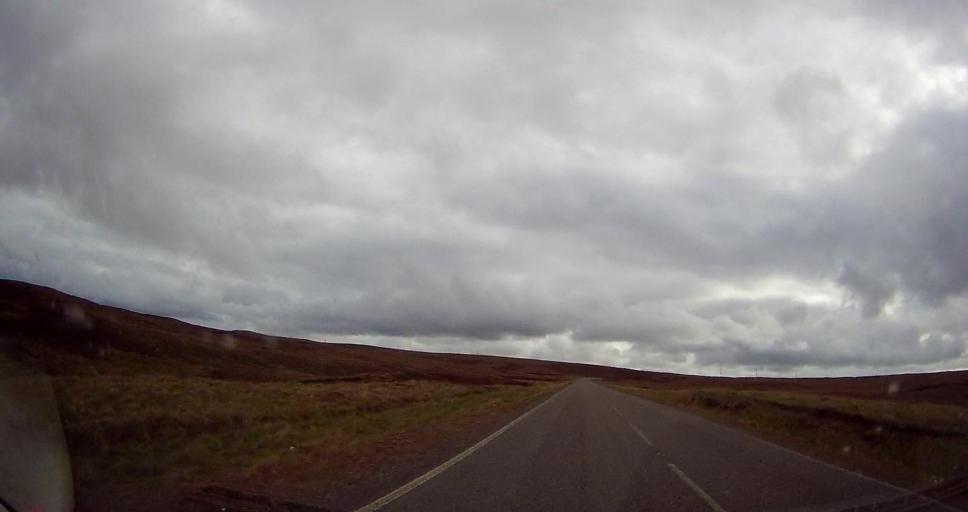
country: GB
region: Scotland
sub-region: Shetland Islands
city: Shetland
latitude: 60.6635
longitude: -1.0398
